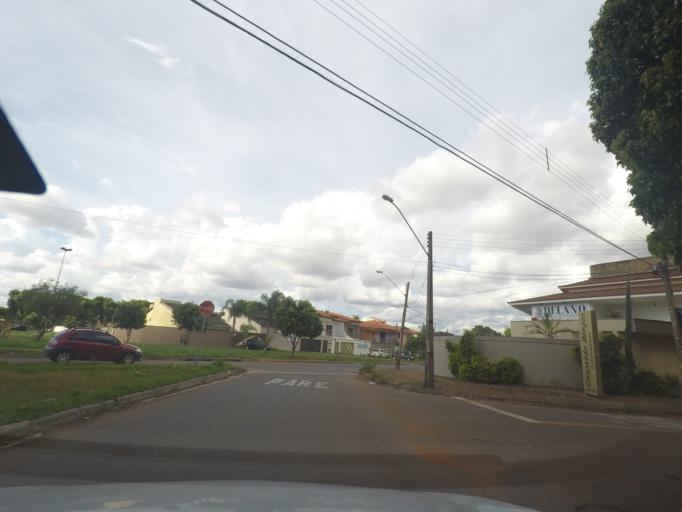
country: BR
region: Goias
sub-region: Goiania
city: Goiania
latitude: -16.7160
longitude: -49.3041
